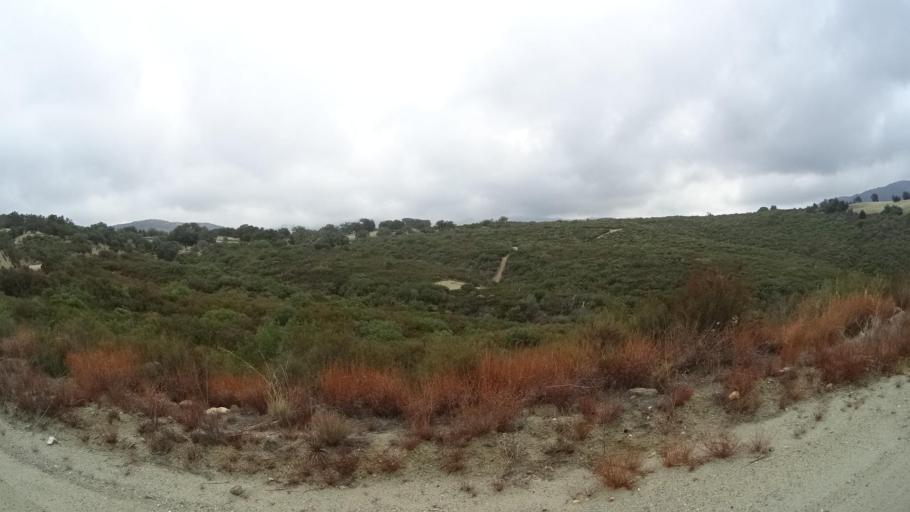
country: US
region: California
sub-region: San Diego County
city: Julian
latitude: 32.9845
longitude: -116.6663
